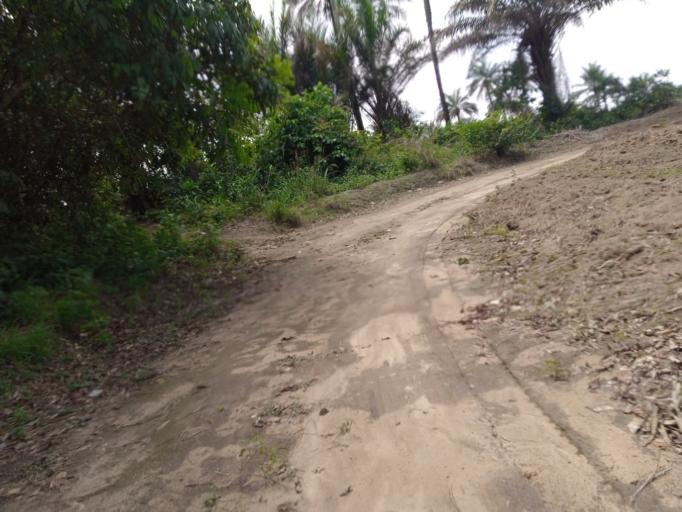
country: SL
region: Western Area
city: Waterloo
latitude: 8.3219
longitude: -13.0105
